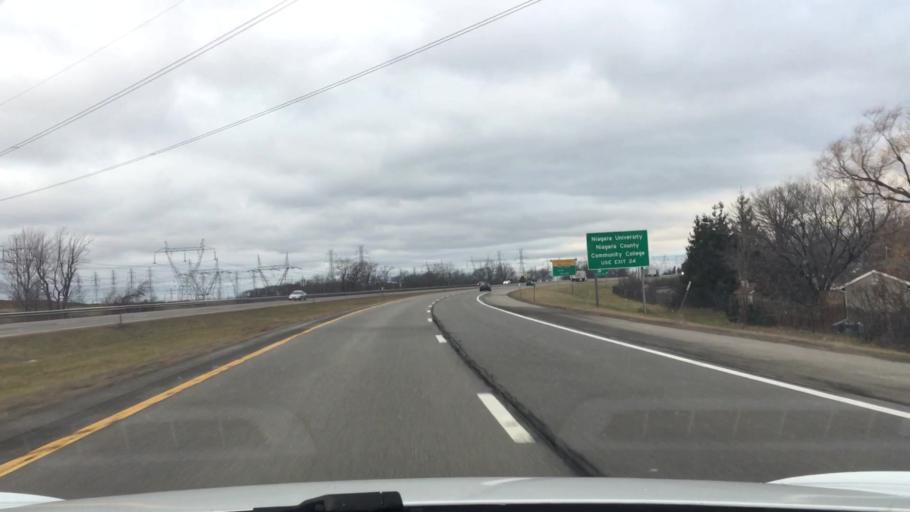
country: US
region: New York
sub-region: Niagara County
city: Niagara Falls
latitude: 43.1238
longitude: -79.0140
